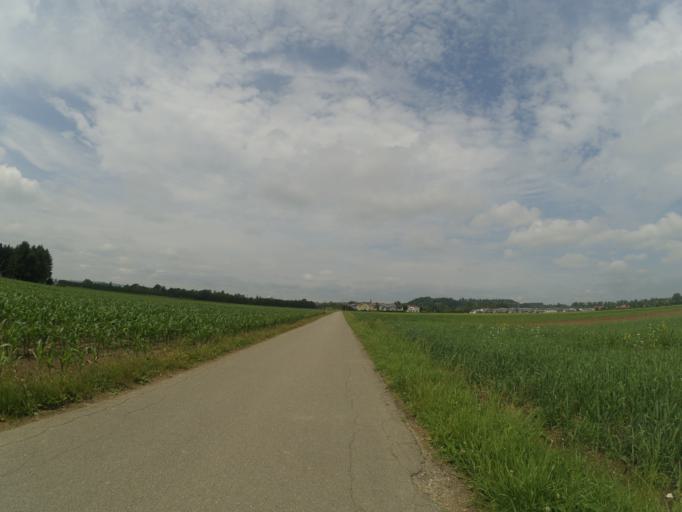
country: DE
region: Baden-Wuerttemberg
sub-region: Tuebingen Region
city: Leutkirch im Allgau
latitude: 47.8128
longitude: 10.0202
